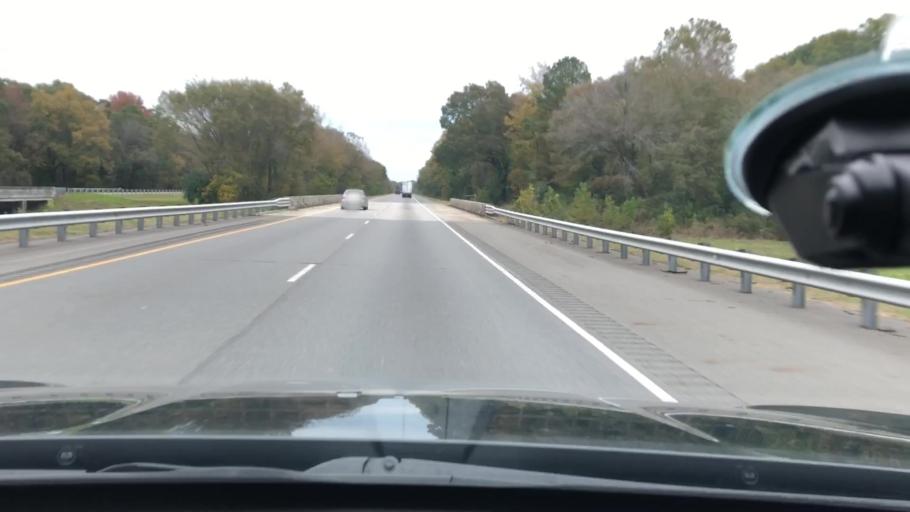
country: US
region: Arkansas
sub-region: Hempstead County
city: Hope
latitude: 33.6538
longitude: -93.6611
